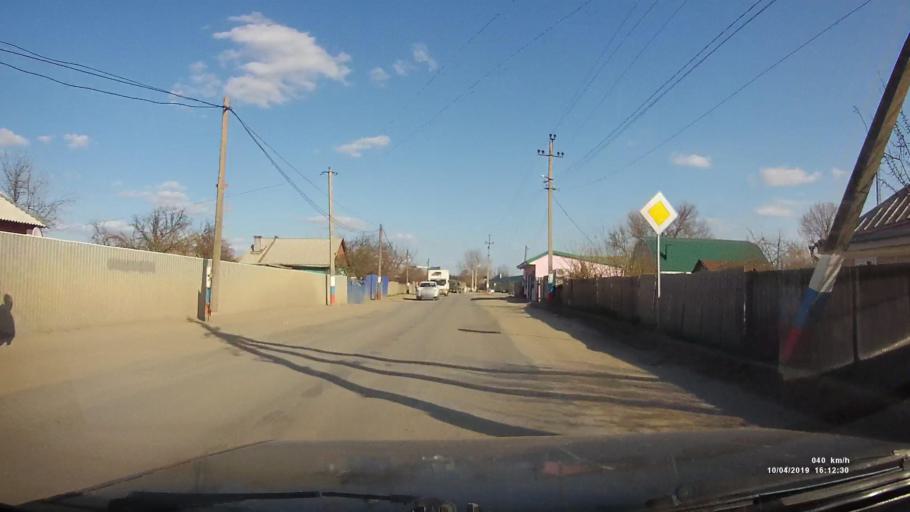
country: RU
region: Rostov
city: Staraya Stanitsa
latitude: 48.3480
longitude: 40.2850
